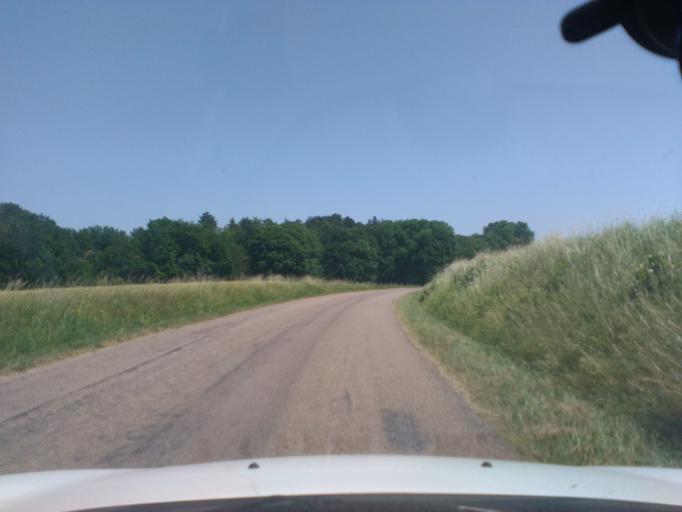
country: FR
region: Lorraine
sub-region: Departement de la Meuse
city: Gondrecourt-le-Chateau
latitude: 48.4249
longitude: 5.5343
